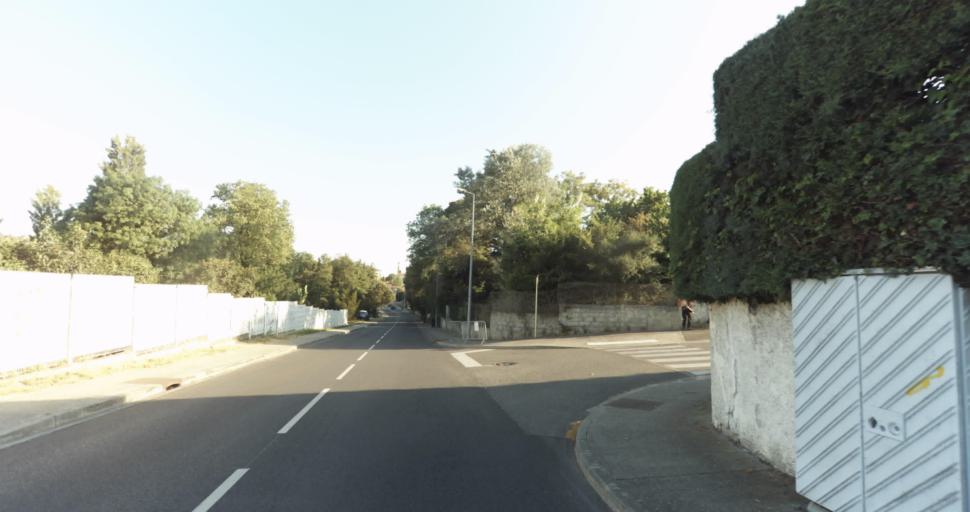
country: FR
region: Midi-Pyrenees
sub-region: Departement de la Haute-Garonne
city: Leguevin
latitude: 43.5952
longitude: 1.2353
